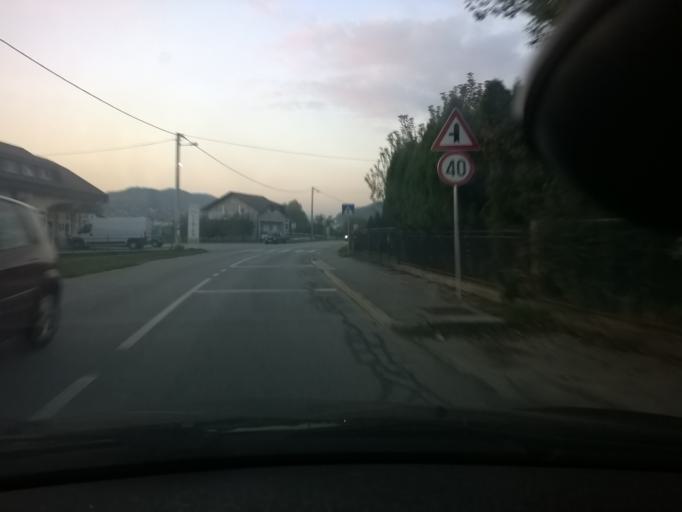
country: HR
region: Krapinsko-Zagorska
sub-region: Grad Krapina
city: Krapina
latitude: 46.1475
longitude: 15.8807
